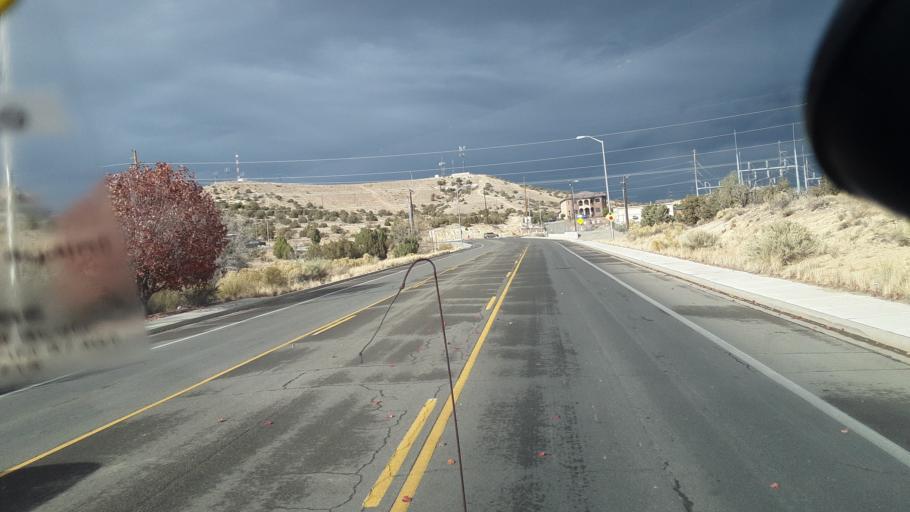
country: US
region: New Mexico
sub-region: San Juan County
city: Farmington
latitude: 36.7723
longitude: -108.1853
